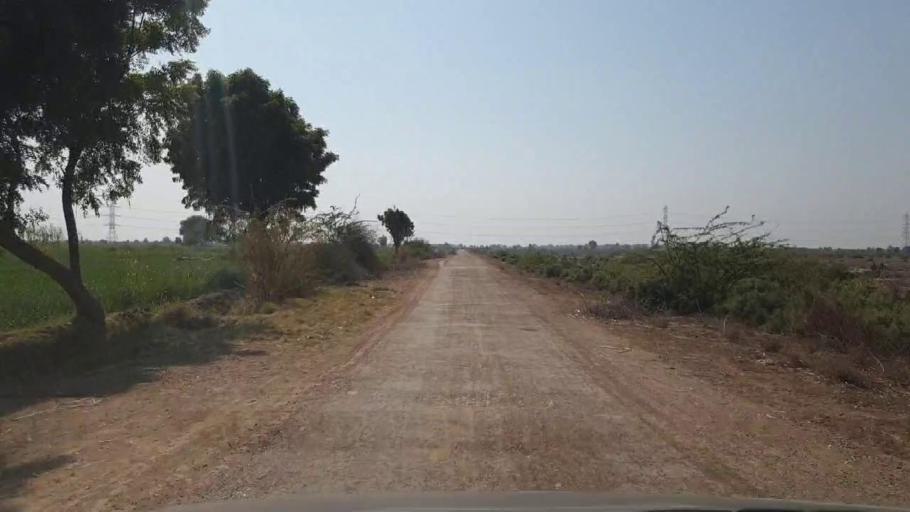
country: PK
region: Sindh
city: Digri
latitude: 25.1929
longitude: 69.2240
